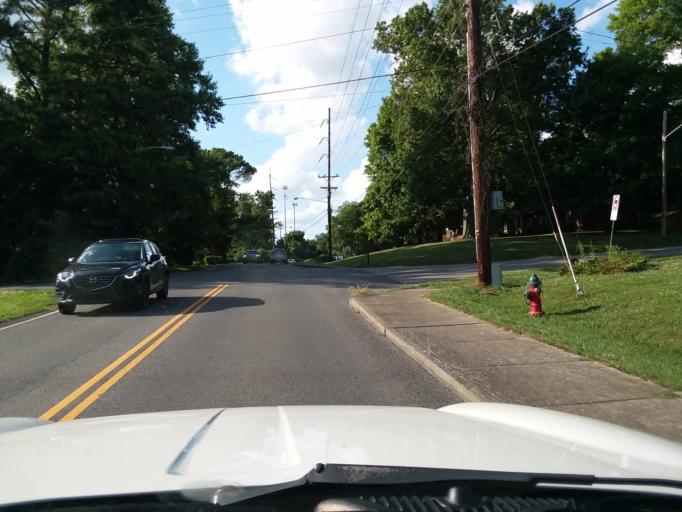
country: US
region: Tennessee
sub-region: Davidson County
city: Oak Hill
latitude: 36.0732
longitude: -86.7591
